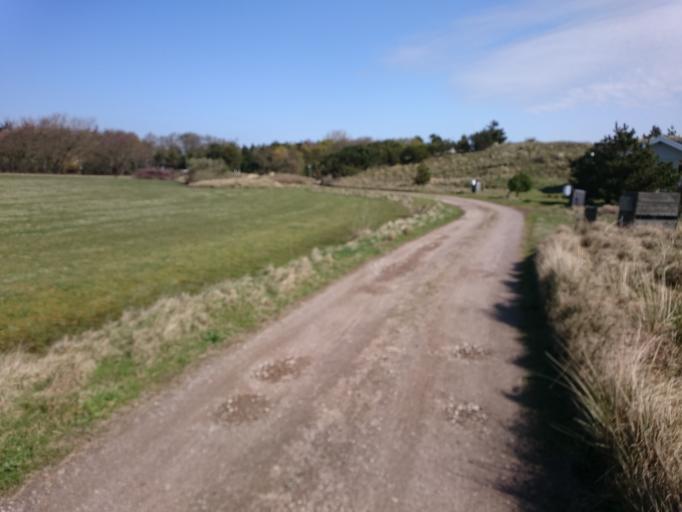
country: DK
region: South Denmark
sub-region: Fano Kommune
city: Nordby
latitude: 55.4406
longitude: 8.3820
